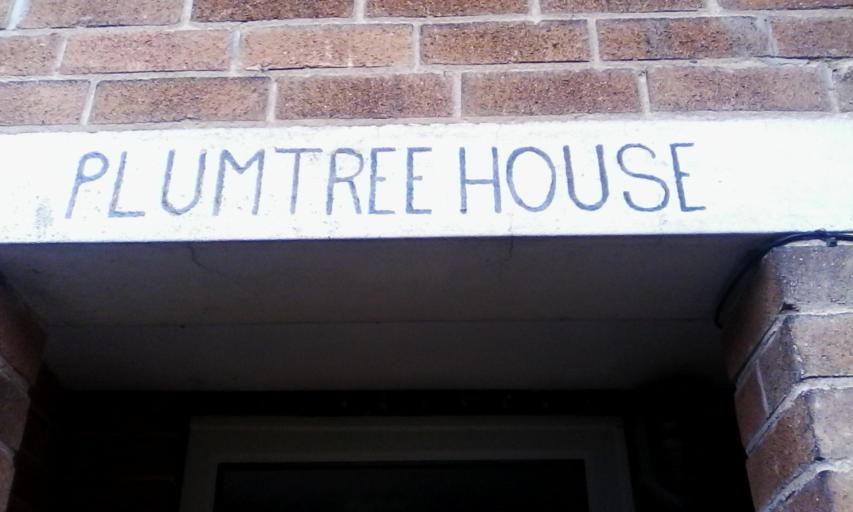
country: GB
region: England
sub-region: Nottinghamshire
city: West Bridgford
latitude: 52.9686
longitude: -1.0955
